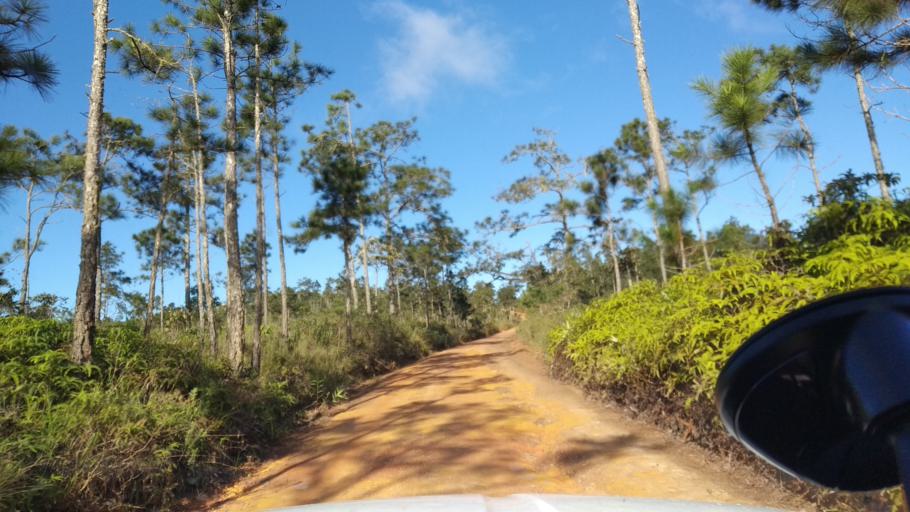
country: BZ
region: Cayo
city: Belmopan
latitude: 16.9977
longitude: -88.8446
